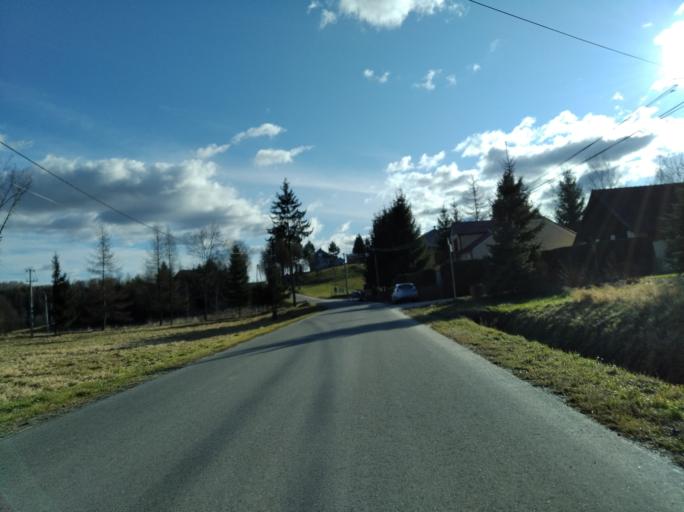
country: PL
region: Subcarpathian Voivodeship
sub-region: Powiat strzyzowski
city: Wisniowa
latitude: 49.8886
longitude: 21.7145
